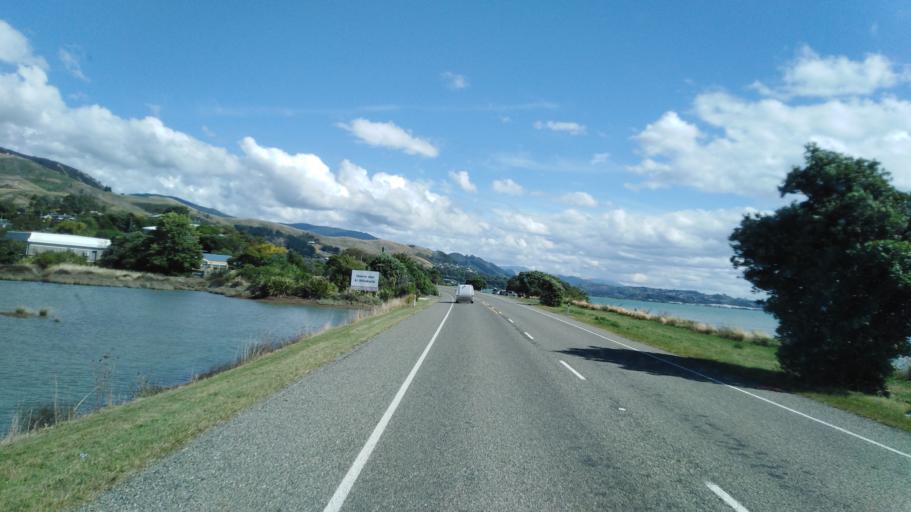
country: NZ
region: Nelson
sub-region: Nelson City
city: Nelson
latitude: -41.2349
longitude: 173.3171
